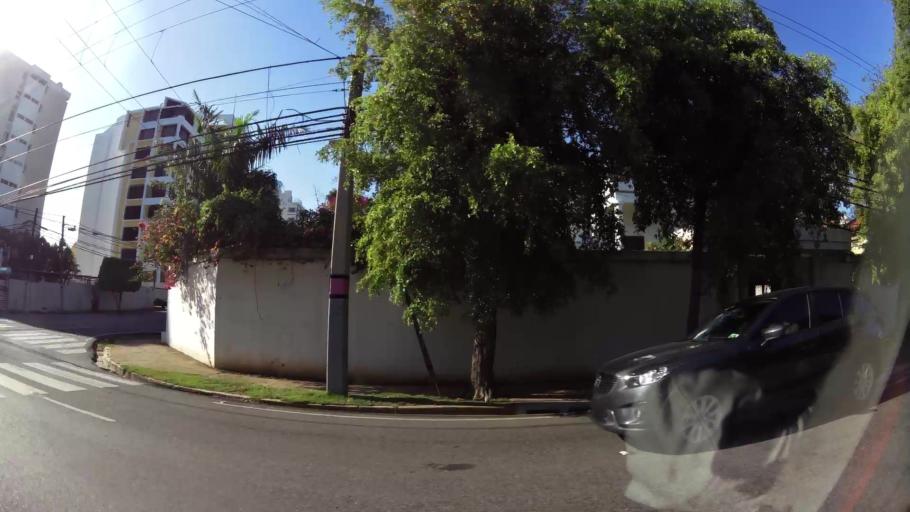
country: DO
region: Nacional
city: Bella Vista
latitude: 18.4407
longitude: -69.9642
